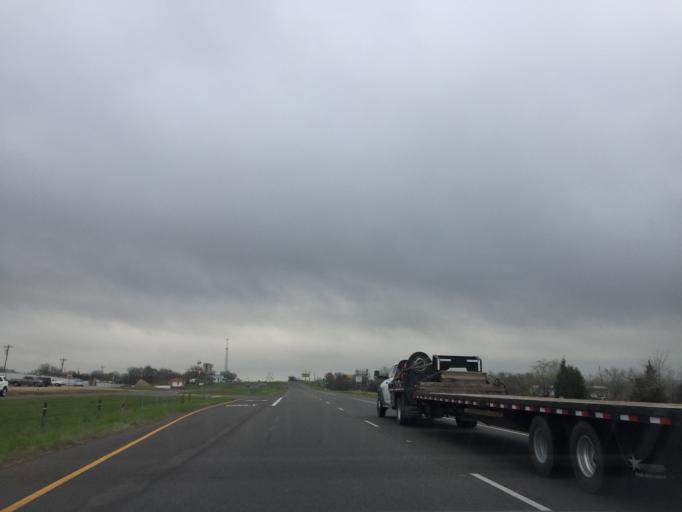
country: US
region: Texas
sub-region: Travis County
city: Garfield
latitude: 30.1883
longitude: -97.5668
